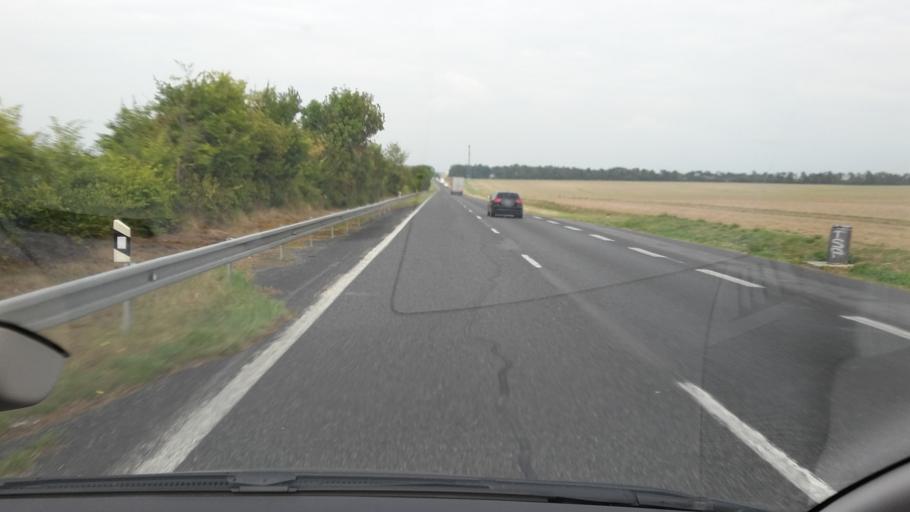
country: FR
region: Champagne-Ardenne
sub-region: Departement de la Marne
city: Warmeriville
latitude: 49.3765
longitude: 4.2213
